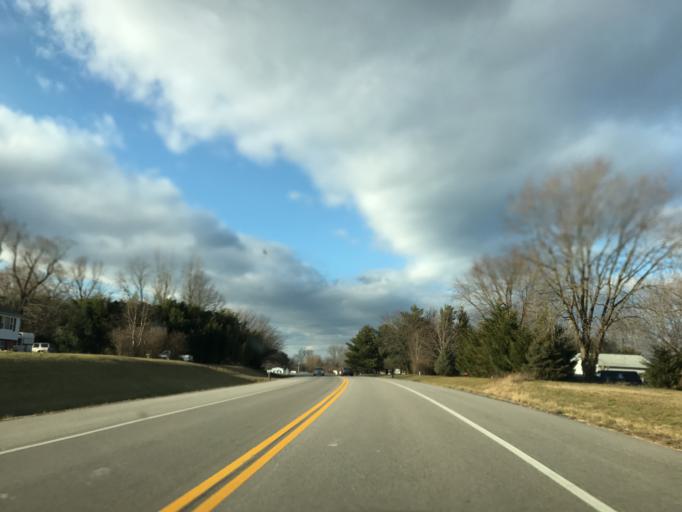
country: US
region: Maryland
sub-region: Cecil County
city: Rising Sun
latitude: 39.6667
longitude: -76.0156
